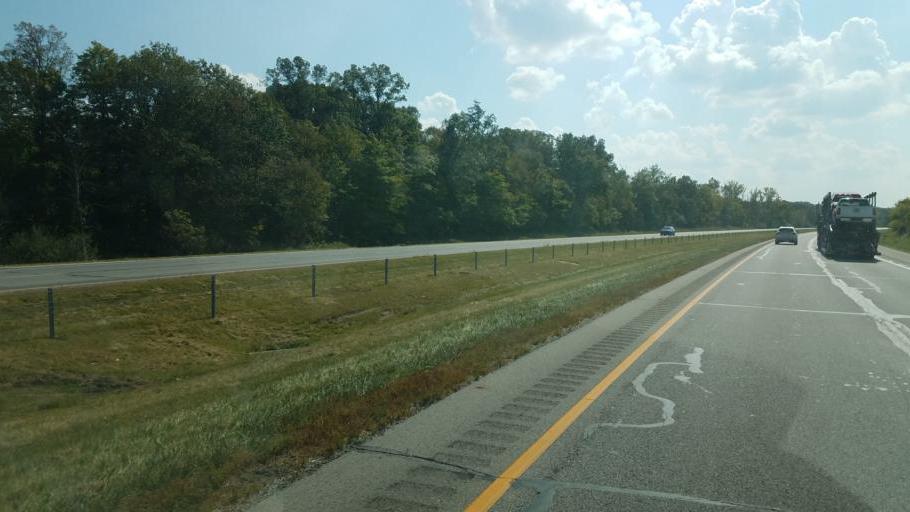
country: US
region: Indiana
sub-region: Allen County
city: Leo-Cedarville
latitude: 41.2589
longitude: -85.0870
